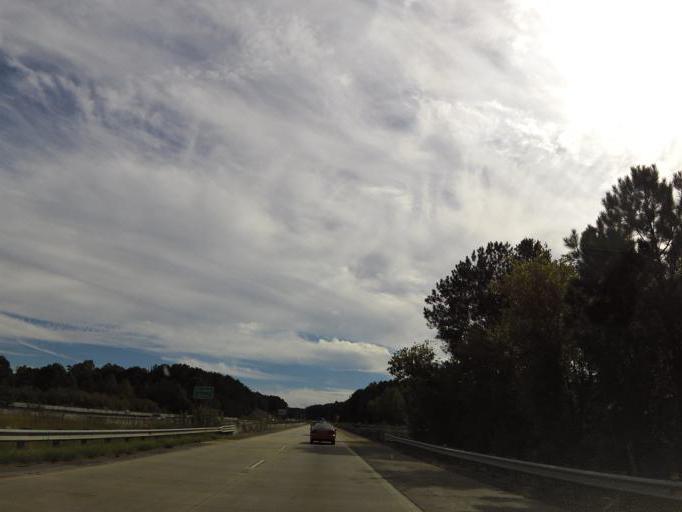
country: US
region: Georgia
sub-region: Cherokee County
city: Canton
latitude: 34.2523
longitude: -84.4675
